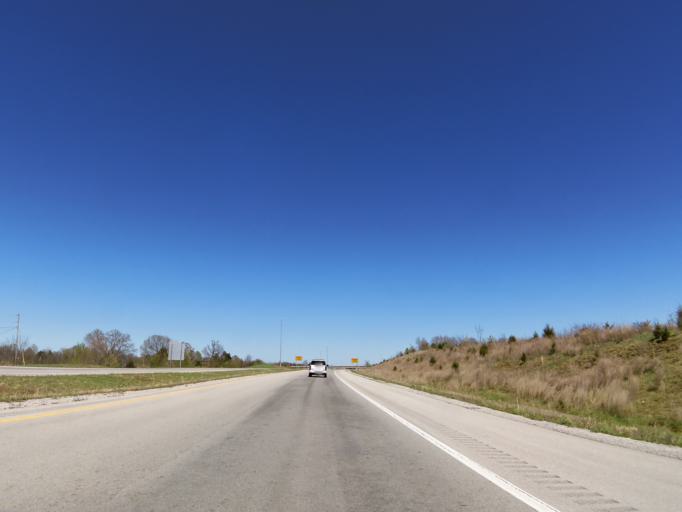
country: US
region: Kentucky
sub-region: Pulaski County
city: Somerset
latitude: 37.1203
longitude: -84.6479
